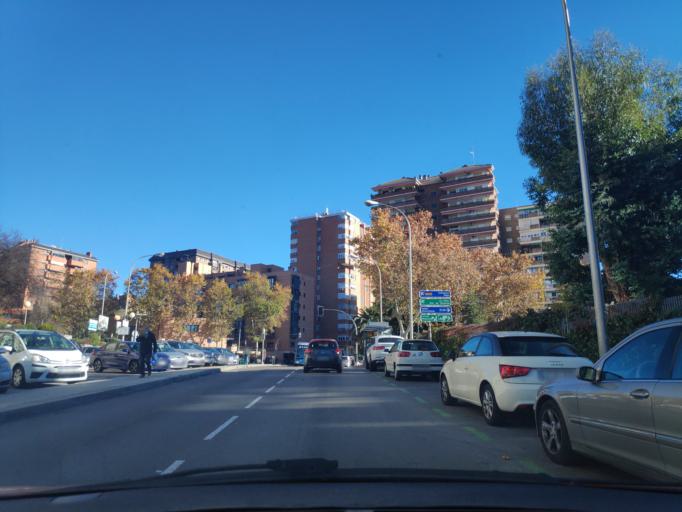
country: ES
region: Madrid
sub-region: Provincia de Madrid
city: Tetuan de las Victorias
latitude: 40.4836
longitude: -3.7078
